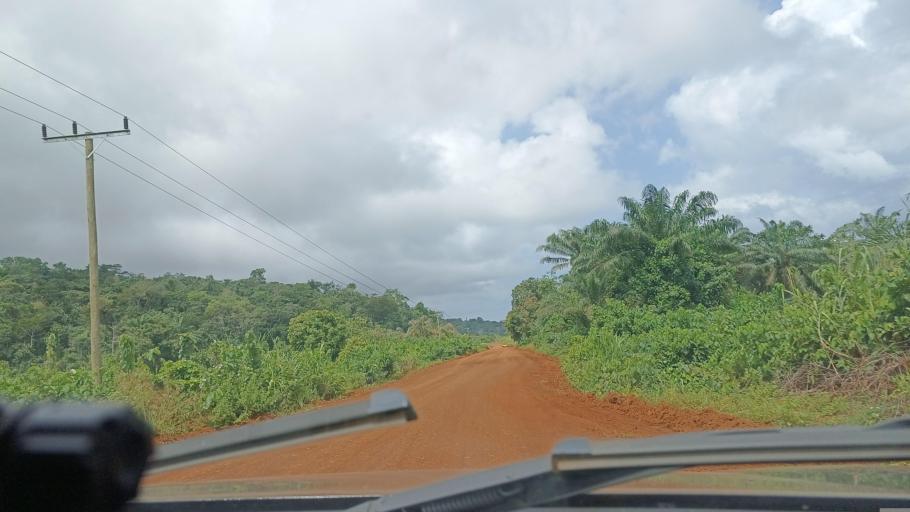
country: LR
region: Grand Cape Mount
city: Robertsport
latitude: 6.7474
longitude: -11.3531
